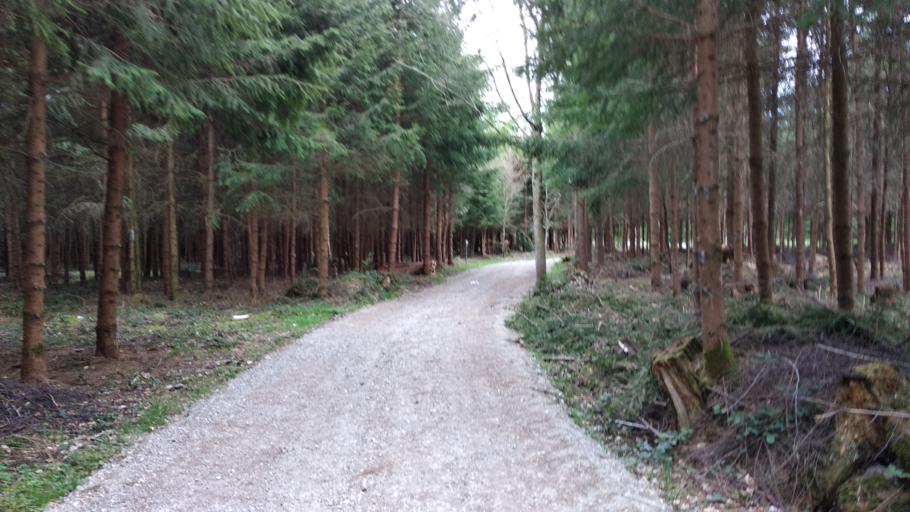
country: DE
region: Bavaria
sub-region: Swabia
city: Woringen
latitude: 47.9248
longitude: 10.1895
